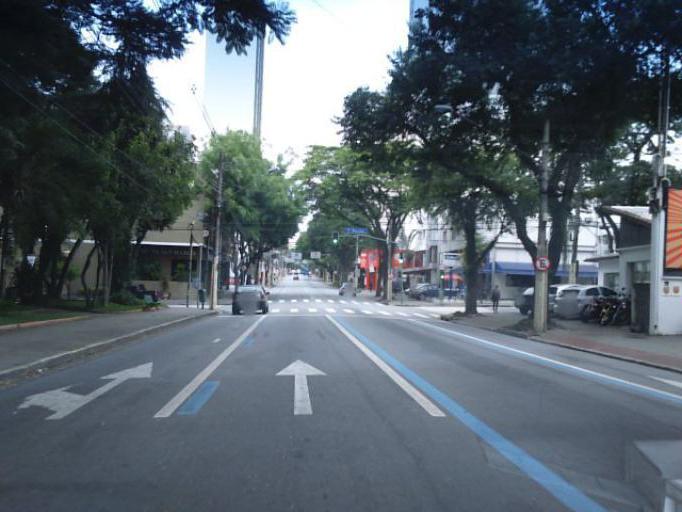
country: BR
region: Sao Paulo
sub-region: Sao Jose Dos Campos
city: Sao Jose dos Campos
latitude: -23.1957
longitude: -45.8910
